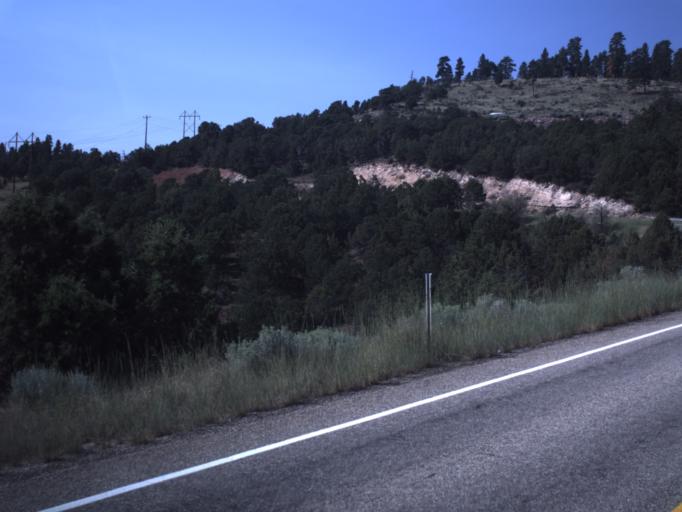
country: US
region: Utah
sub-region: Daggett County
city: Manila
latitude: 40.8982
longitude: -109.4461
